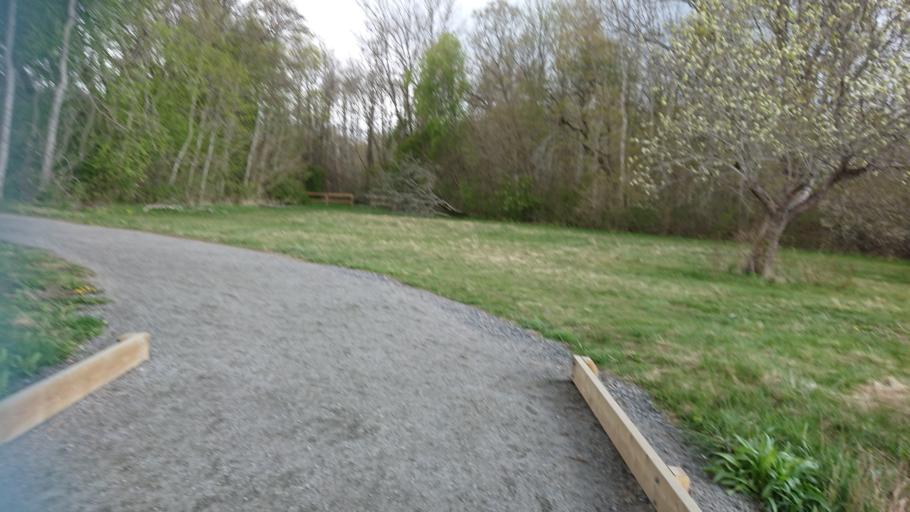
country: SE
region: Uppsala
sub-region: Uppsala Kommun
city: Uppsala
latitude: 59.7991
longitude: 17.6078
